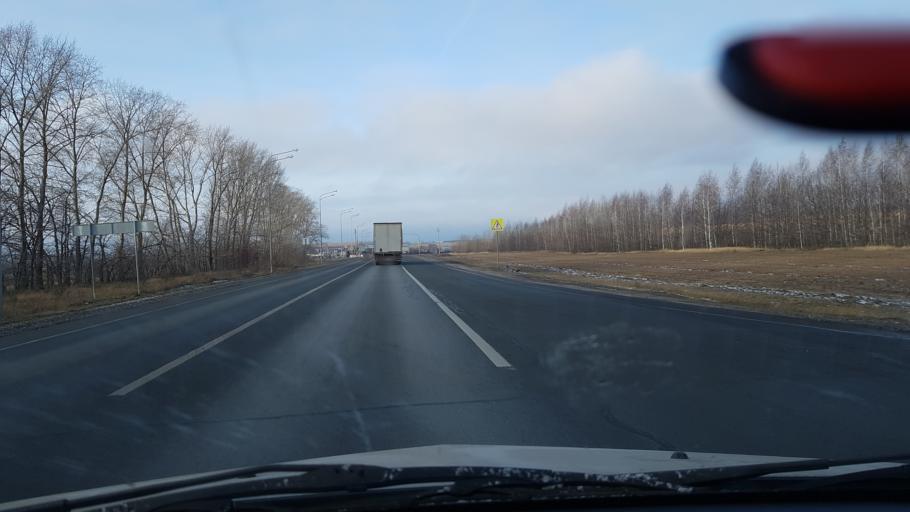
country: RU
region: Tatarstan
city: Laishevo
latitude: 55.3908
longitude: 49.8115
